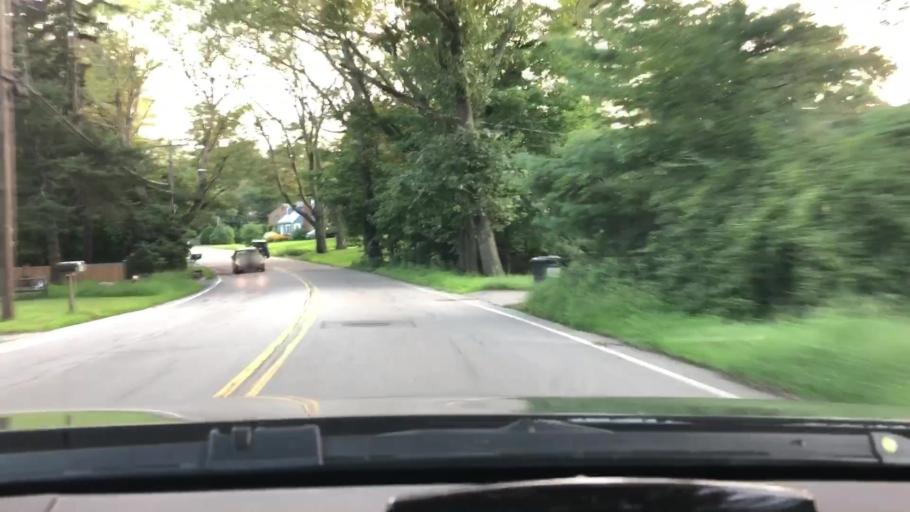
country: US
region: Massachusetts
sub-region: Norfolk County
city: Millis-Clicquot
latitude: 42.1609
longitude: -71.3490
